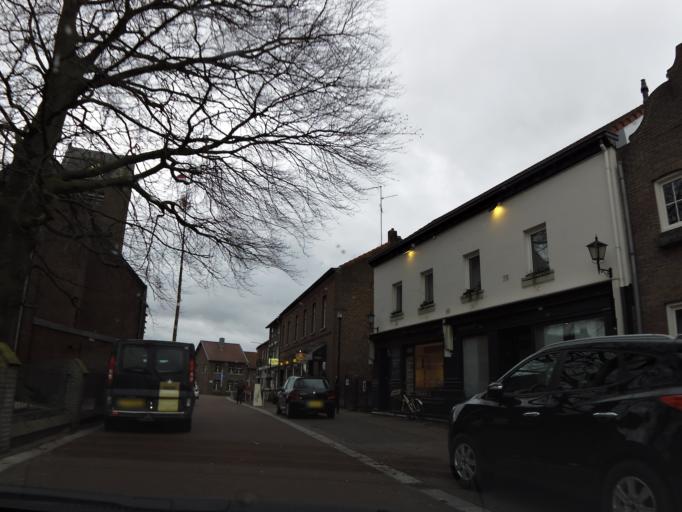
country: NL
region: Limburg
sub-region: Eijsden-Margraten
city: Margraten
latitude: 50.7903
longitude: 5.8094
